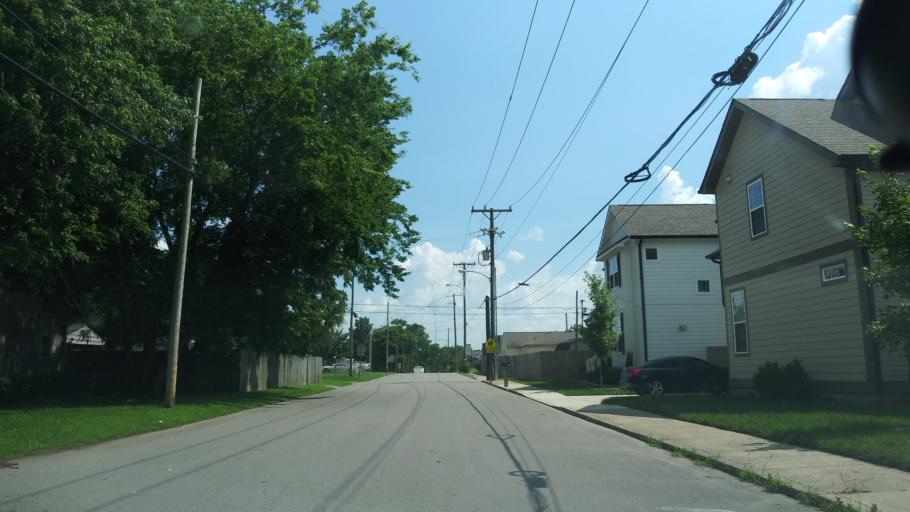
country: US
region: Tennessee
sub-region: Davidson County
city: Belle Meade
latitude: 36.1572
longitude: -86.8464
